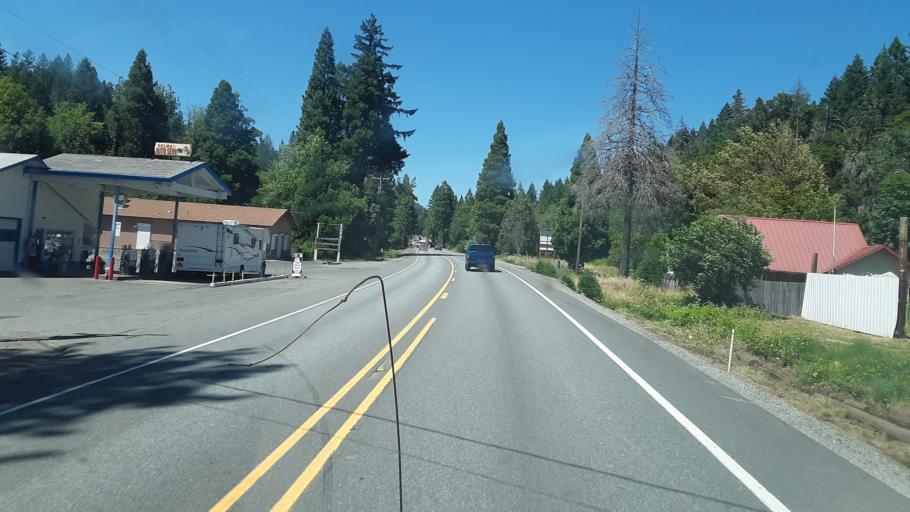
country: US
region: Oregon
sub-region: Josephine County
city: Cave Junction
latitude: 42.2890
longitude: -123.6125
